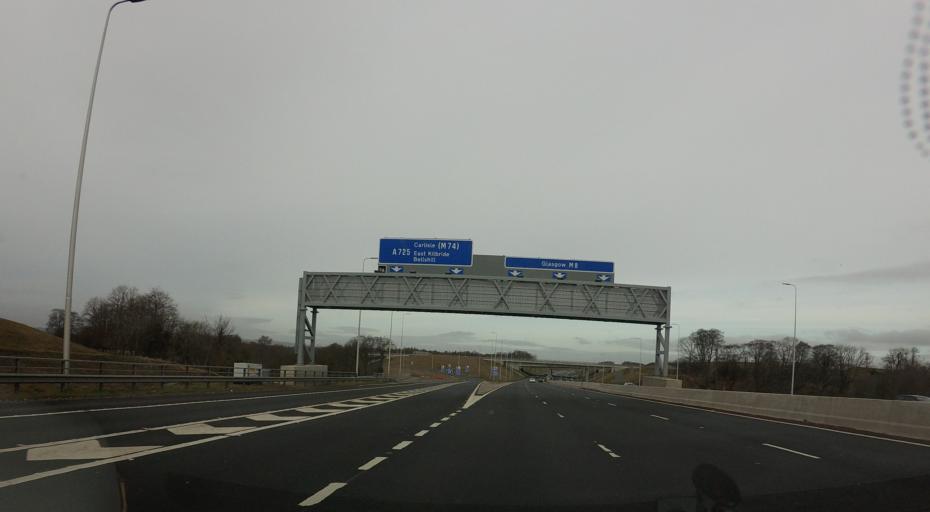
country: GB
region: Scotland
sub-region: North Lanarkshire
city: Bellshill
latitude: 55.8373
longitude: -4.0175
